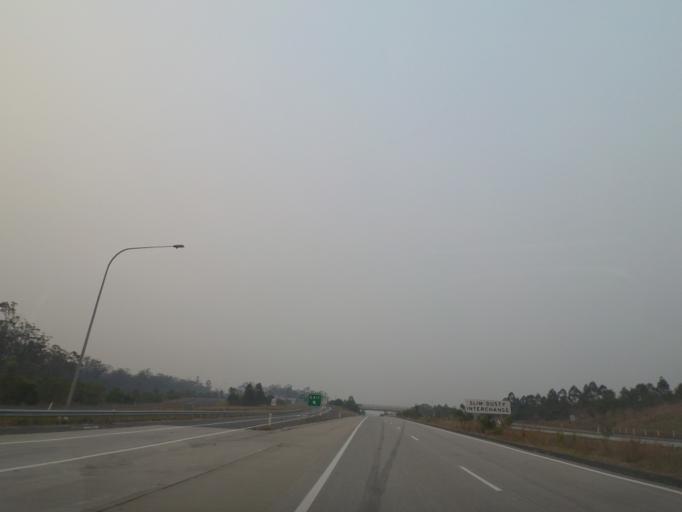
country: AU
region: New South Wales
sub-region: Kempsey
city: Kempsey
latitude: -31.1300
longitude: 152.8257
